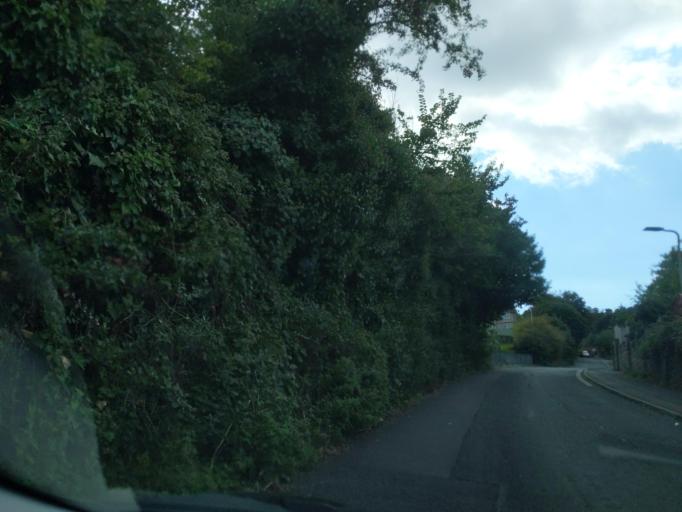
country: GB
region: England
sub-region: Plymouth
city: Plymstock
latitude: 50.3523
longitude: -4.1095
